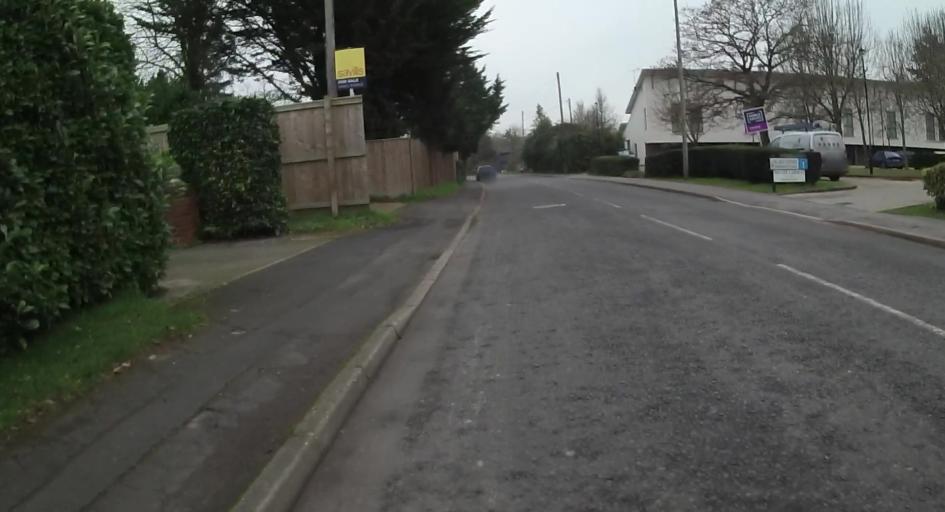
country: GB
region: England
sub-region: Hampshire
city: Kings Worthy
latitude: 51.1050
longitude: -1.3047
